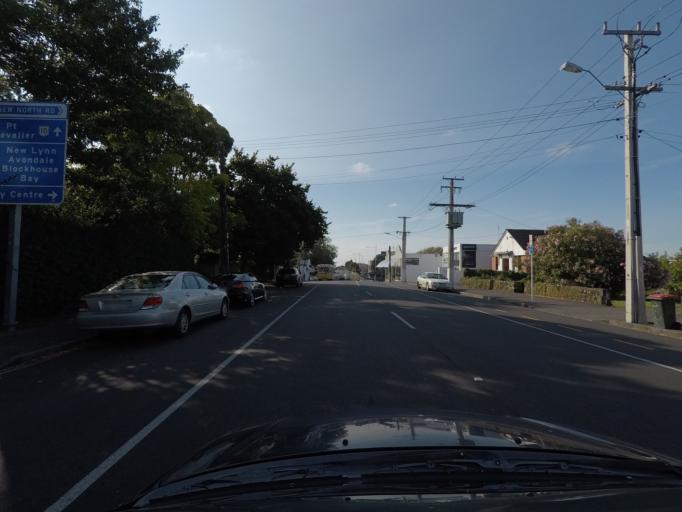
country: NZ
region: Auckland
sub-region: Auckland
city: Rosebank
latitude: -36.8847
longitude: 174.7165
